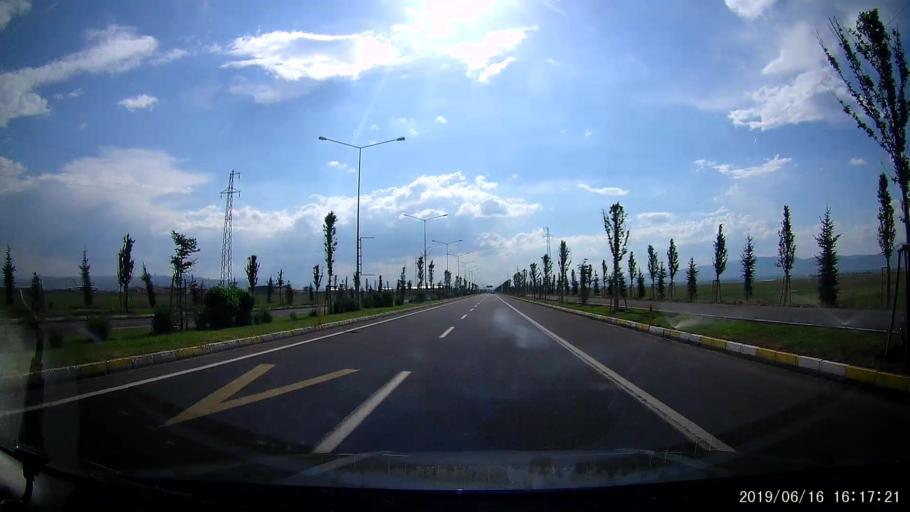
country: TR
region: Erzurum
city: Ilica
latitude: 39.9638
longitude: 41.1887
